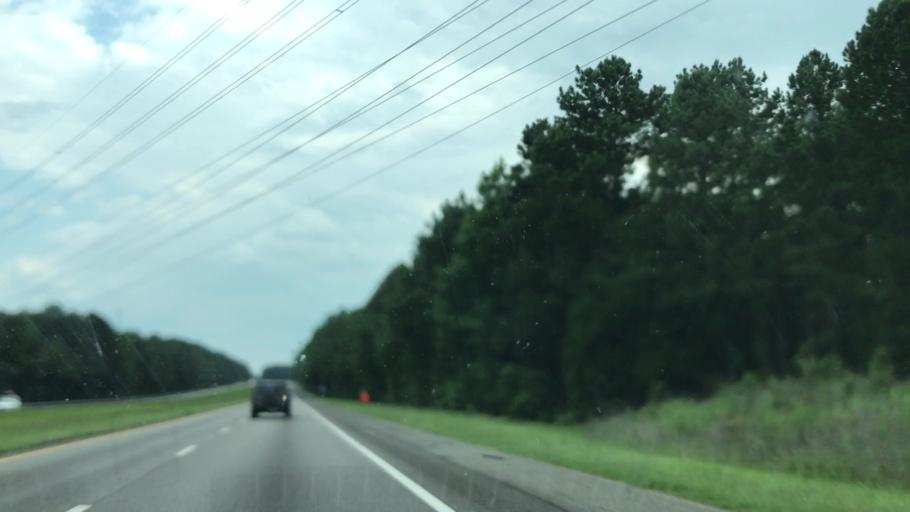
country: US
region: South Carolina
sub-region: Richland County
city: Blythewood
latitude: 34.2740
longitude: -80.9979
